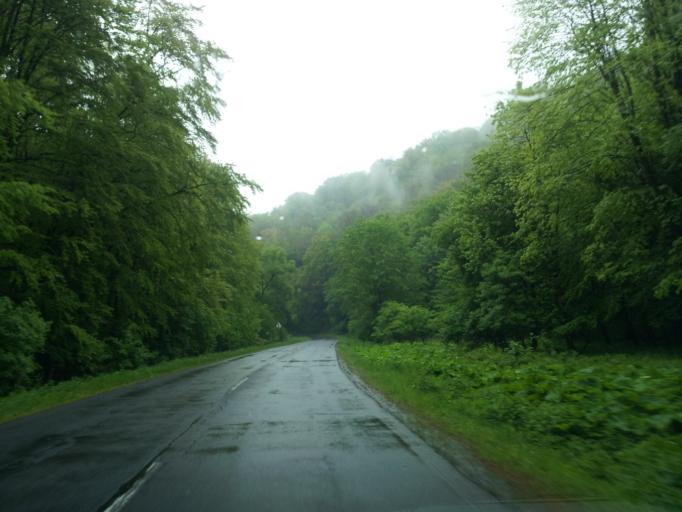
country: HU
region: Baranya
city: Komlo
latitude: 46.2052
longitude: 18.2999
